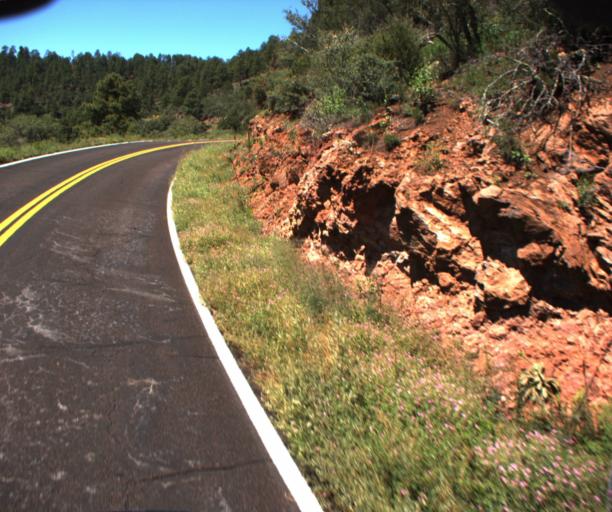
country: US
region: Arizona
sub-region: Greenlee County
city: Morenci
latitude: 33.4631
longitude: -109.3652
